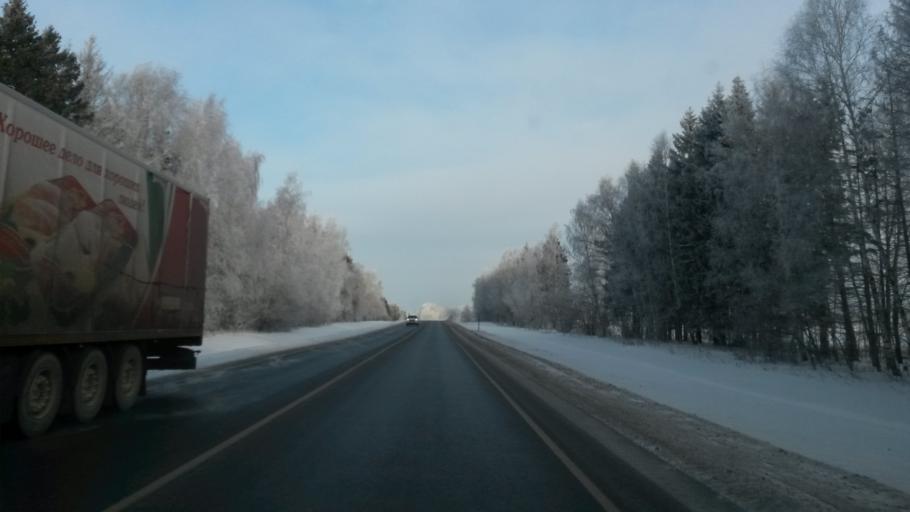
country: RU
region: Vladimir
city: Bogolyubovo
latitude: 56.2362
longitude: 40.4502
